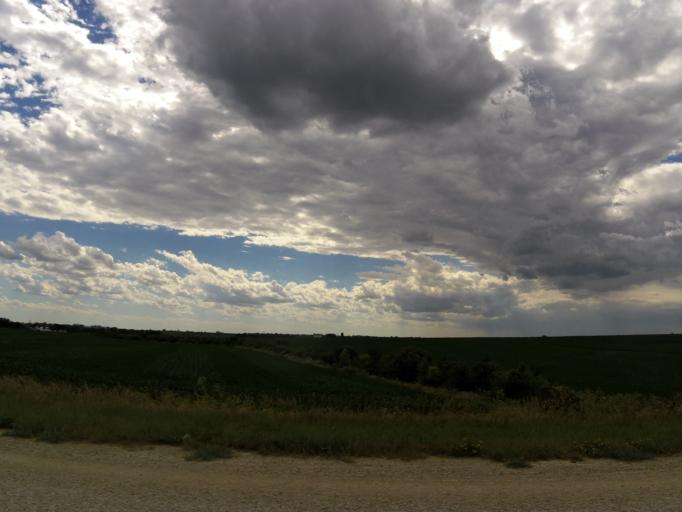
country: US
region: Iowa
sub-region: Henry County
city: Mount Pleasant
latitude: 40.8058
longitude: -91.5648
